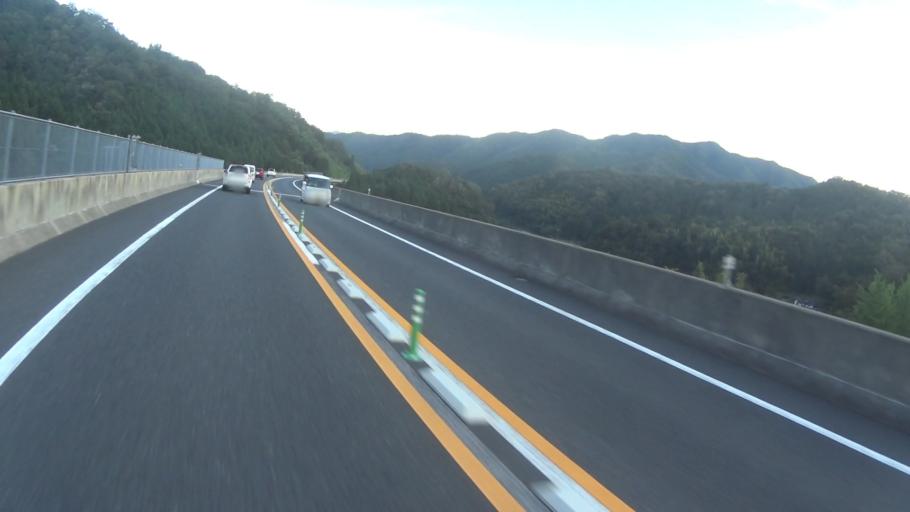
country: JP
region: Kyoto
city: Miyazu
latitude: 35.4487
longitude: 135.1832
